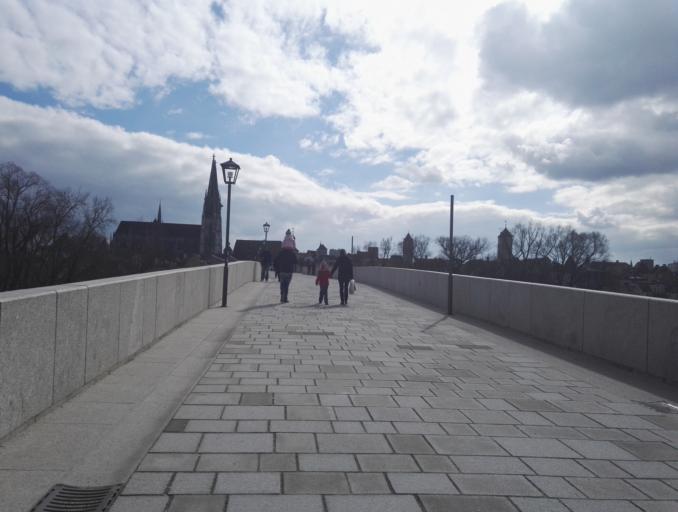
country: DE
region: Bavaria
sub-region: Upper Palatinate
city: Lappersdorf
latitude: 49.0239
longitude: 12.0972
